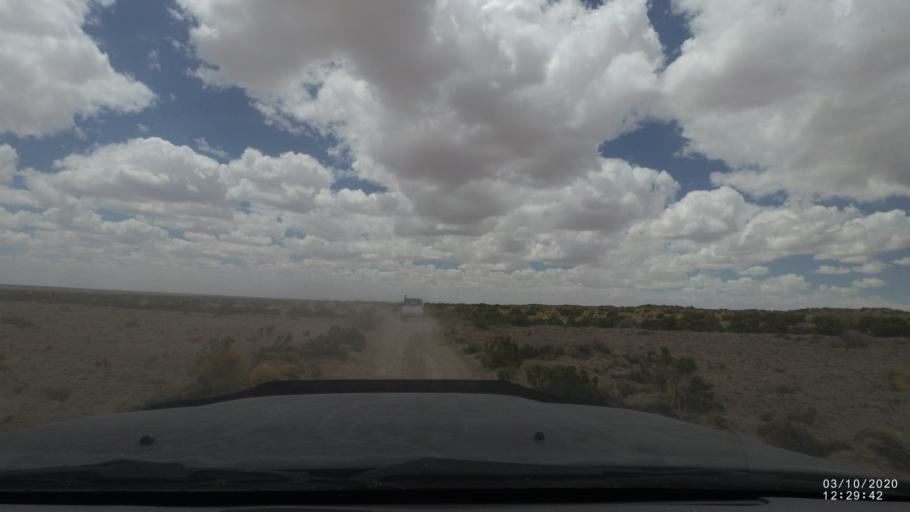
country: BO
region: Oruro
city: Poopo
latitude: -18.6886
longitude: -67.5468
